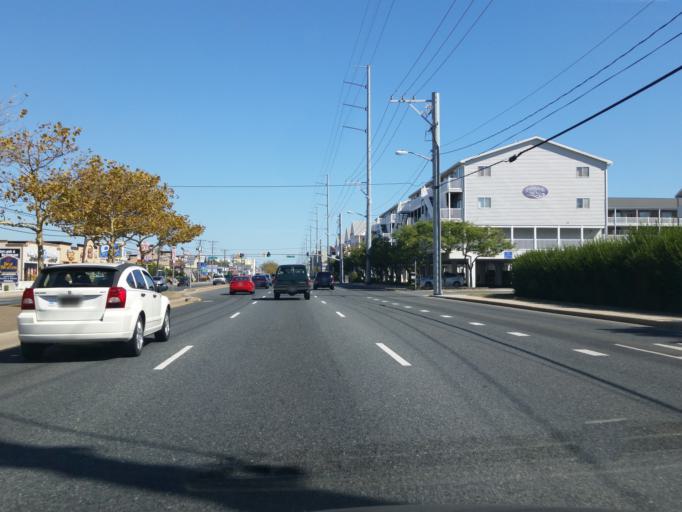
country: US
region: Maryland
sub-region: Worcester County
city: Ocean City
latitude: 38.3790
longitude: -75.0683
